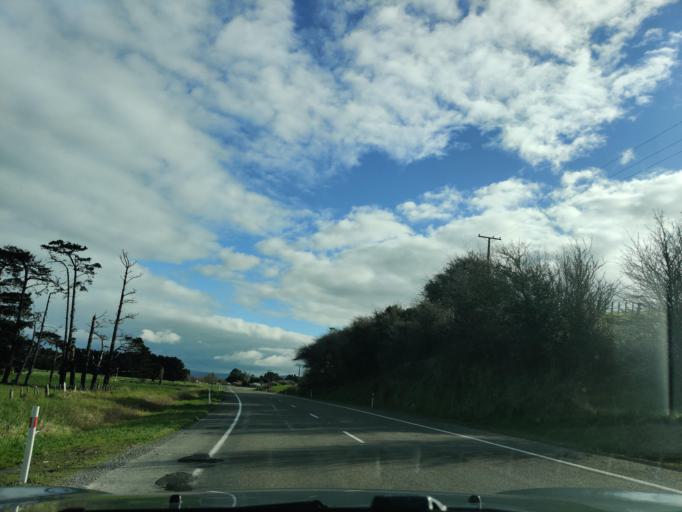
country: NZ
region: Manawatu-Wanganui
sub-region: Palmerston North City
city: Palmerston North
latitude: -40.3392
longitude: 175.8894
